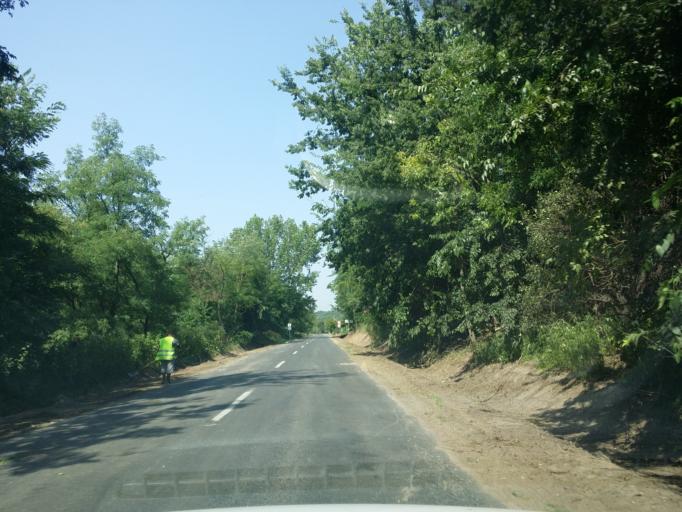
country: HU
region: Tolna
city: Pincehely
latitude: 46.6344
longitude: 18.4145
